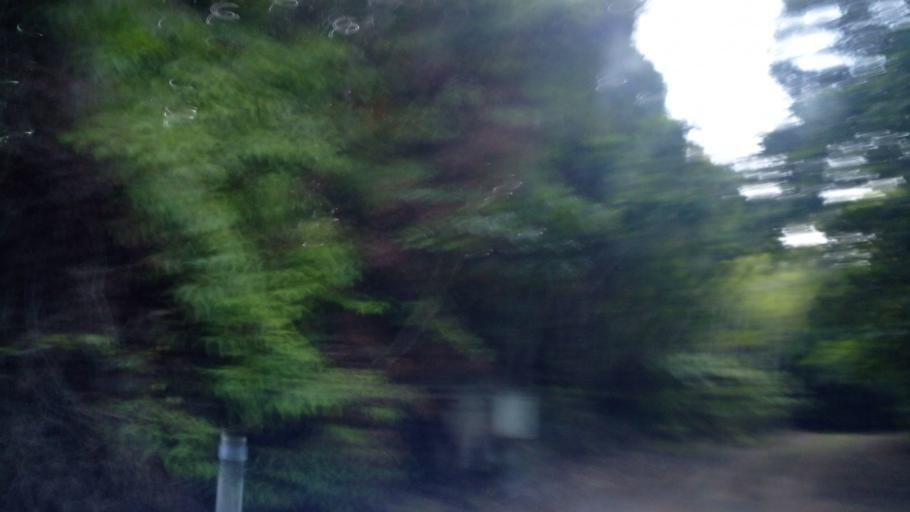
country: AU
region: Queensland
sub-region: Tablelands
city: Atherton
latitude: -17.3737
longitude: 145.7557
